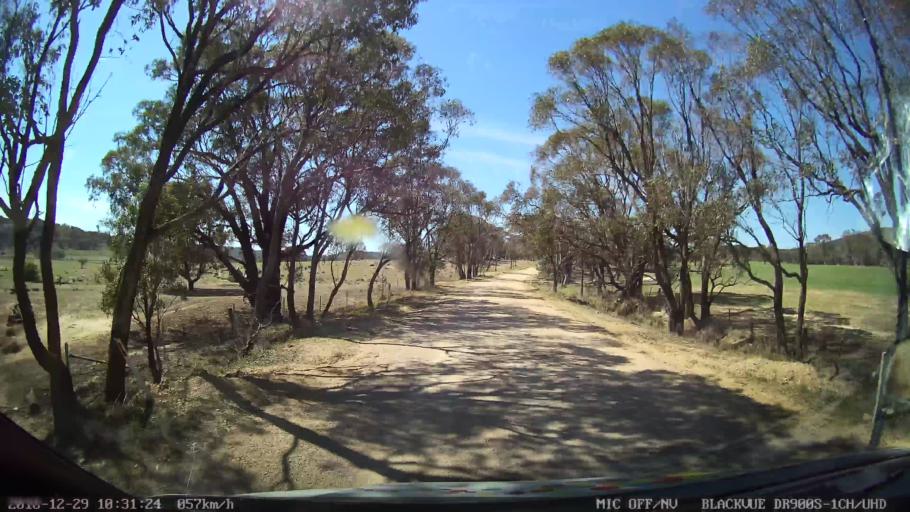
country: AU
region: New South Wales
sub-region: Yass Valley
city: Gundaroo
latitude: -34.9681
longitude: 149.4578
